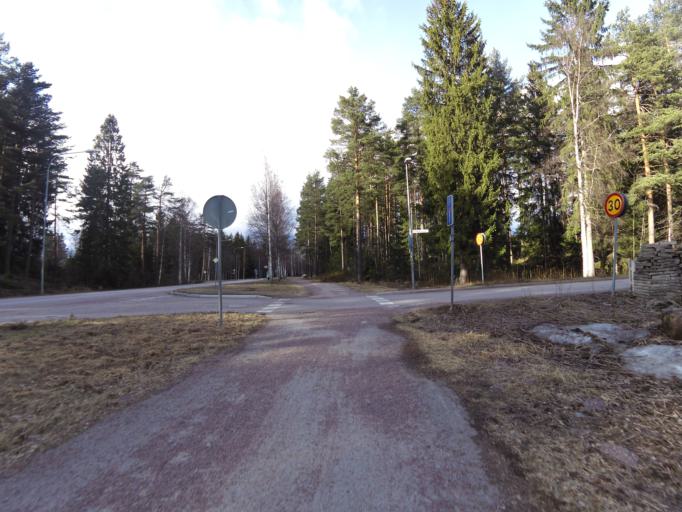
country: SE
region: Gaevleborg
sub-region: Gavle Kommun
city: Gavle
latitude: 60.6877
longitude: 17.0930
